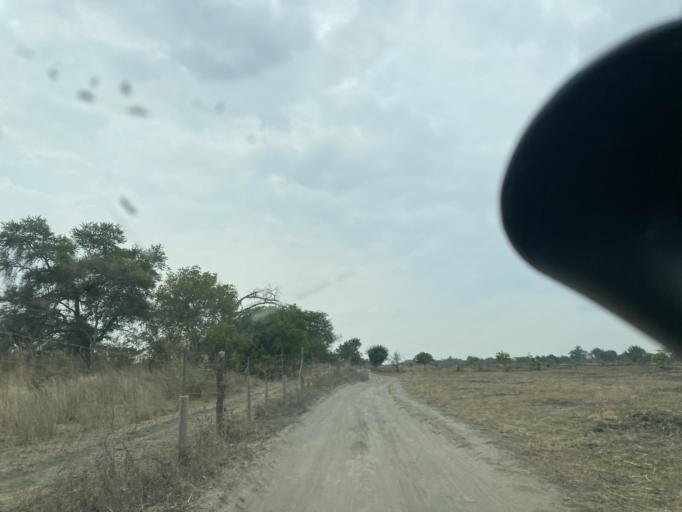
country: ZM
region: Lusaka
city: Lusaka
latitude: -15.2502
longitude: 28.3316
